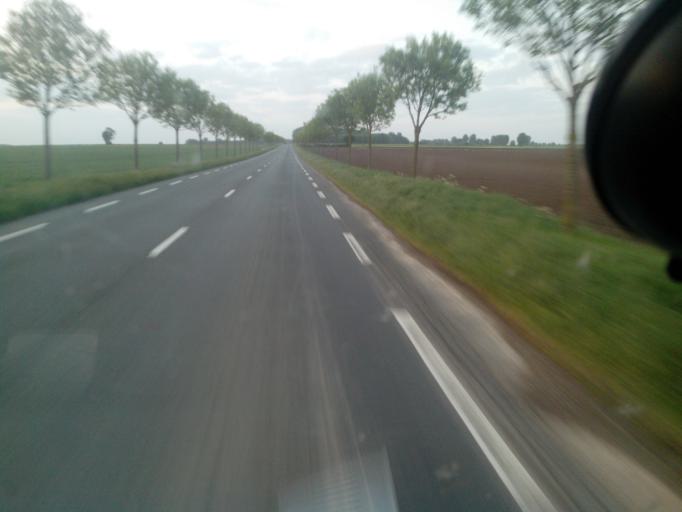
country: FR
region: Nord-Pas-de-Calais
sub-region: Departement du Pas-de-Calais
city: Marconnelle
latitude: 50.2963
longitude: 1.9992
